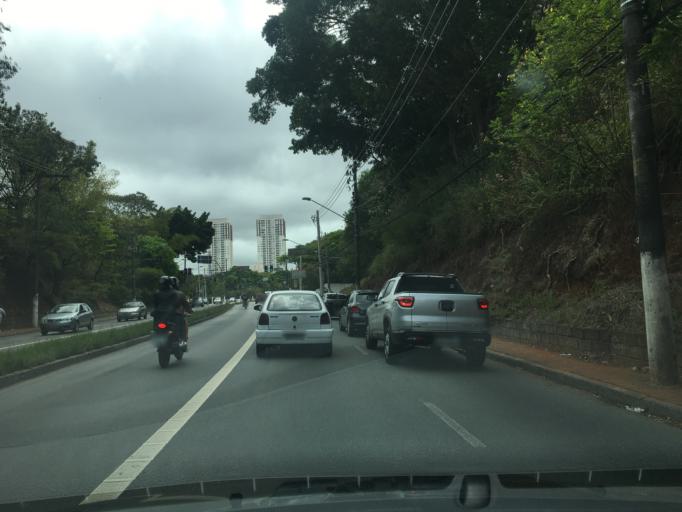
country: BR
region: Sao Paulo
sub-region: Taboao Da Serra
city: Taboao da Serra
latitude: -23.6041
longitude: -46.7451
